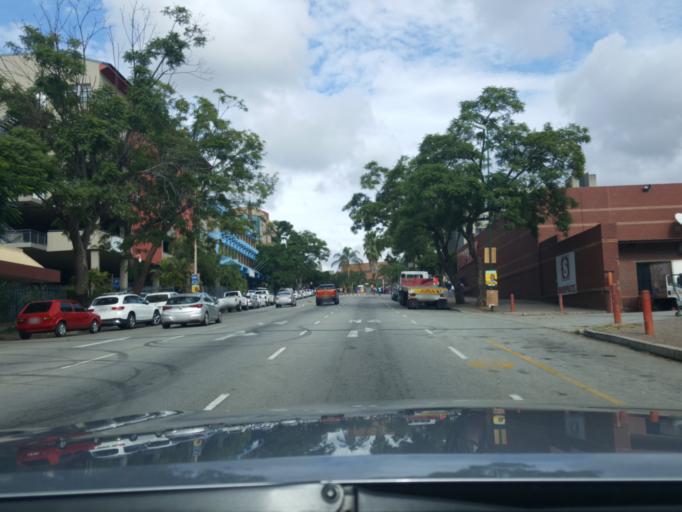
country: ZA
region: Mpumalanga
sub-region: Ehlanzeni District
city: Nelspruit
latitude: -25.4722
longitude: 30.9800
